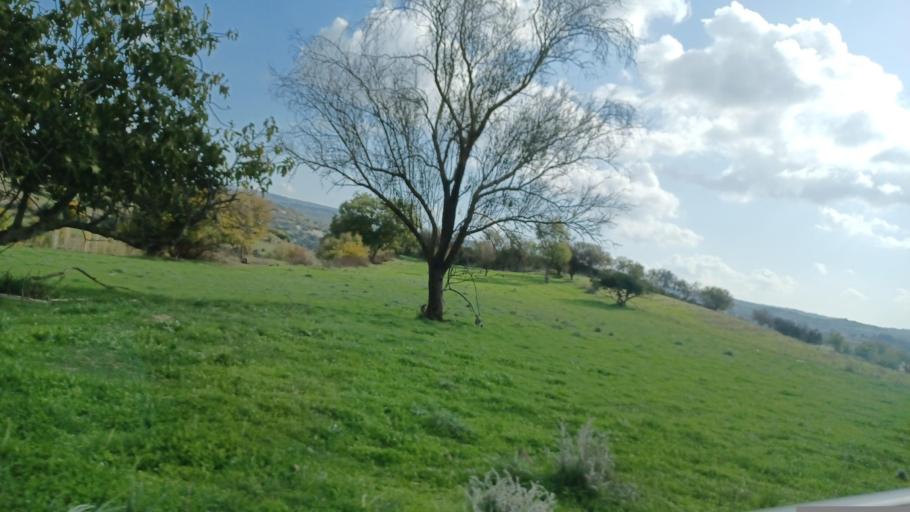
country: CY
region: Pafos
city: Mesogi
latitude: 34.8611
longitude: 32.5382
